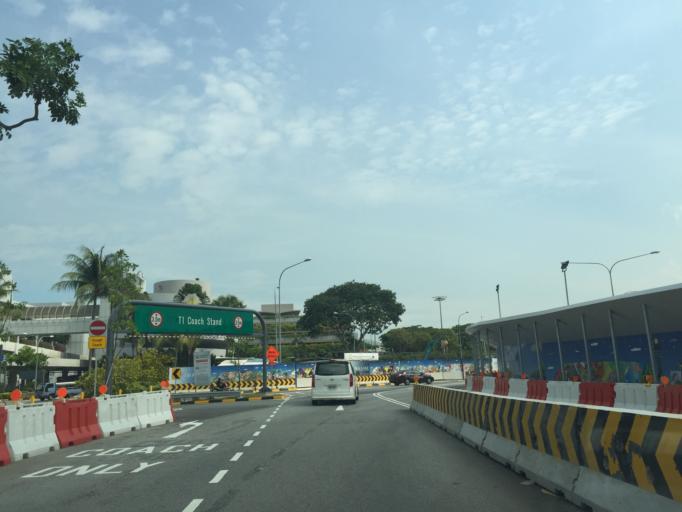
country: SG
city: Singapore
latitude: 1.3596
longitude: 103.9907
